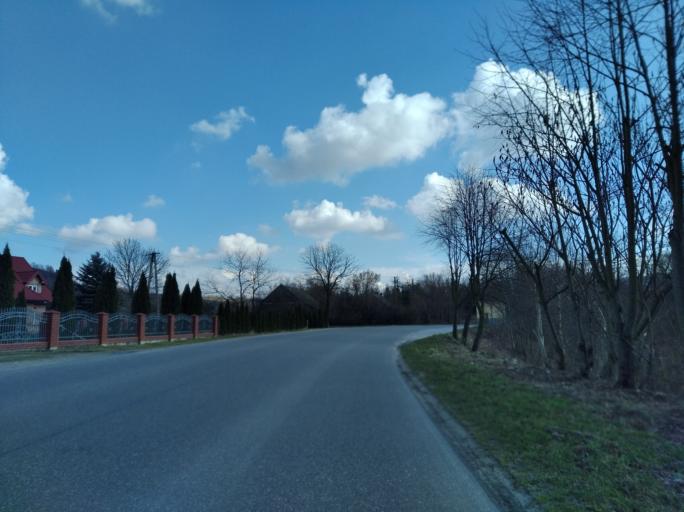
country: PL
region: Subcarpathian Voivodeship
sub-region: Powiat jasielski
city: Kolaczyce
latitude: 49.8587
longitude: 21.4851
